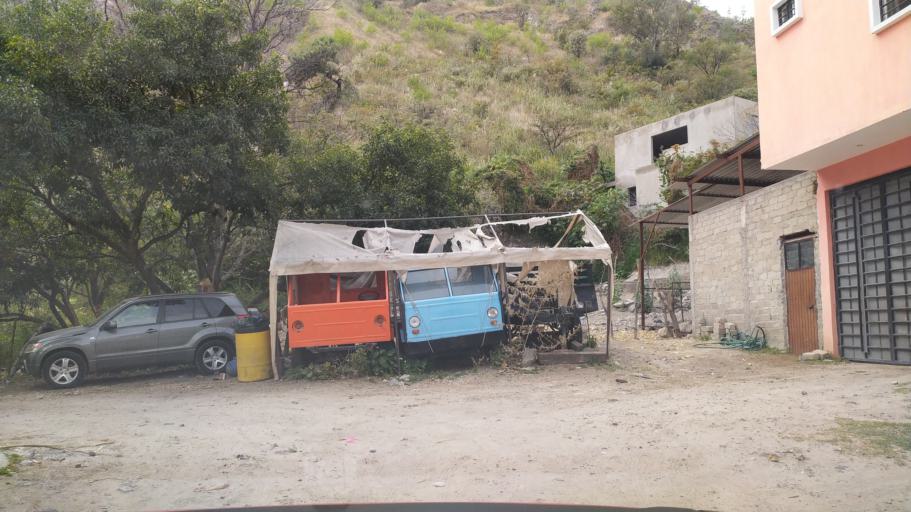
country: MX
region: Jalisco
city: Guadalajara
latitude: 20.6604
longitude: -103.4560
